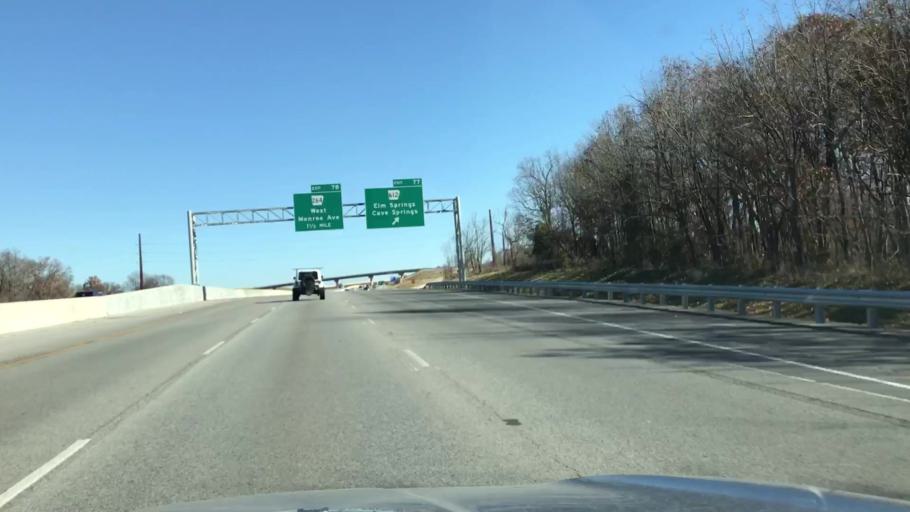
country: US
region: Arkansas
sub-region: Benton County
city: Lowell
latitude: 36.2337
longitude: -94.1699
